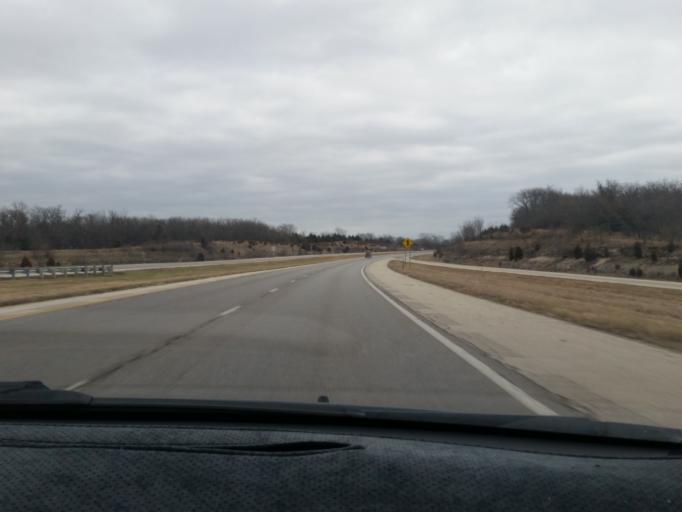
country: US
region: Kansas
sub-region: Johnson County
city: De Soto
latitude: 38.9600
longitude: -95.0186
